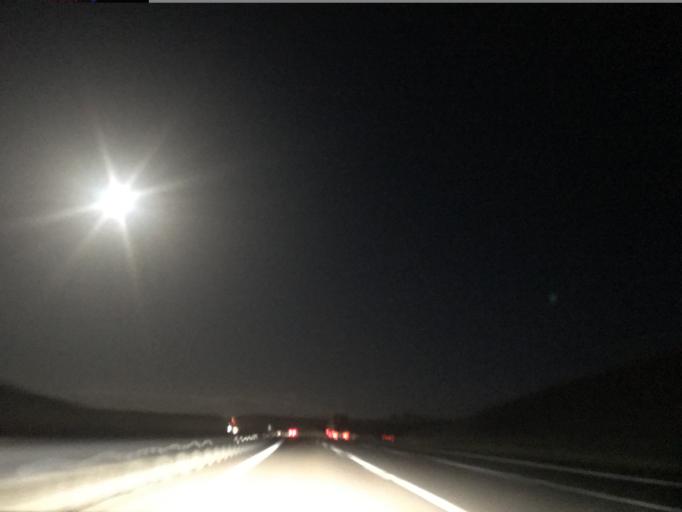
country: TR
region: Nigde
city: Ulukisla
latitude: 37.6411
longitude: 34.3814
